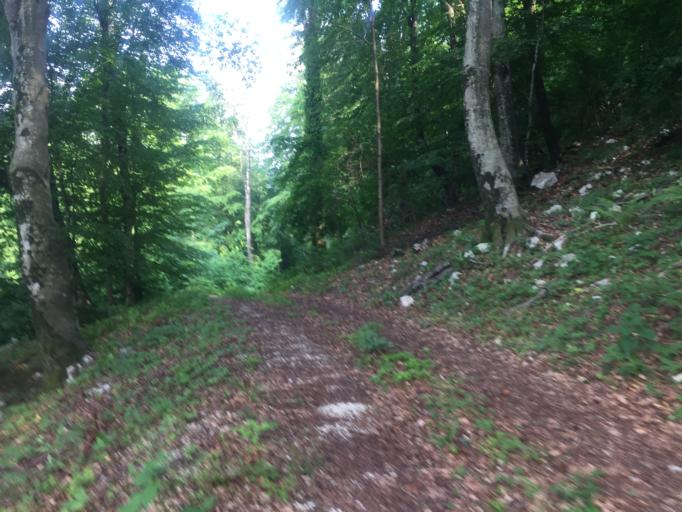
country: IT
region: Friuli Venezia Giulia
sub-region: Provincia di Udine
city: Cavazzo Carnico
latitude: 46.3502
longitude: 13.0204
